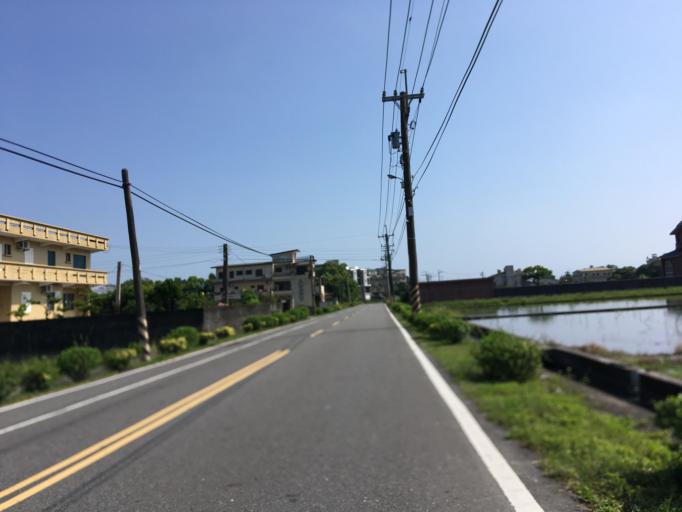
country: TW
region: Taiwan
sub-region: Yilan
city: Yilan
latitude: 24.6831
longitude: 121.7400
